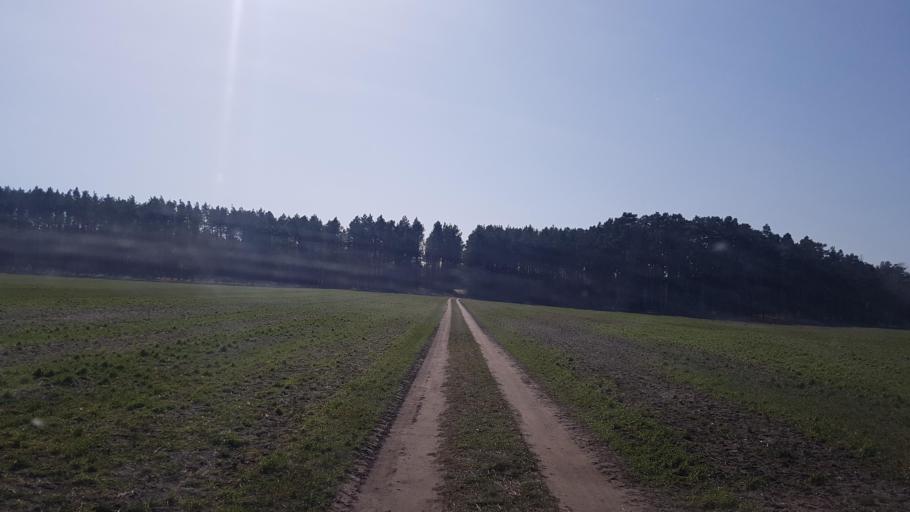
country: DE
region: Brandenburg
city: Schonewalde
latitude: 51.6383
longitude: 13.6232
